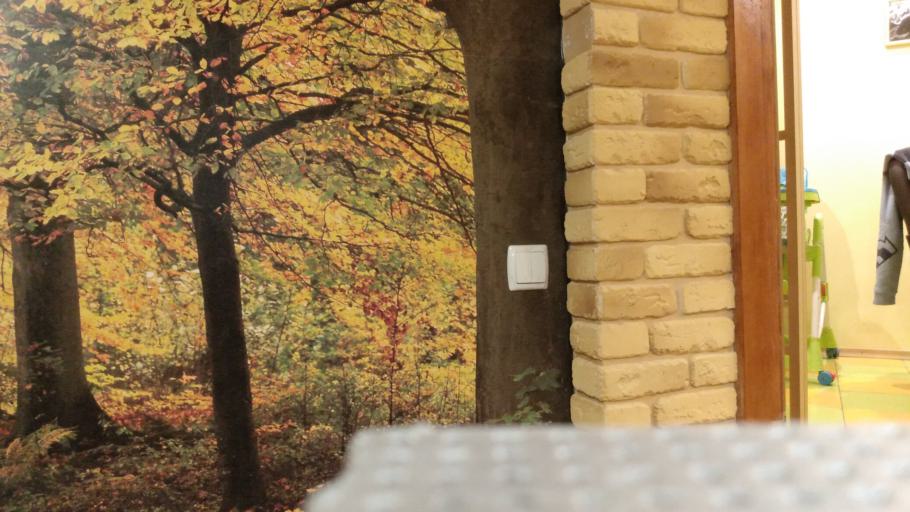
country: RU
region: Vologda
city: Babayevo
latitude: 59.3710
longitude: 35.9946
